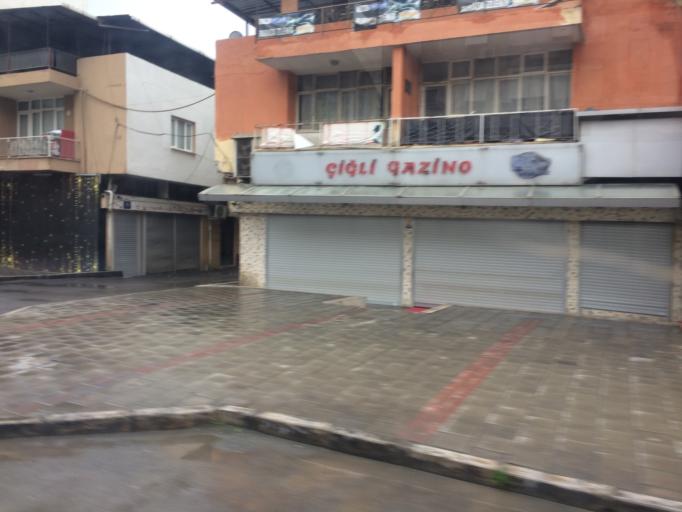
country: TR
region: Izmir
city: Karsiyaka
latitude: 38.4983
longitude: 27.0572
